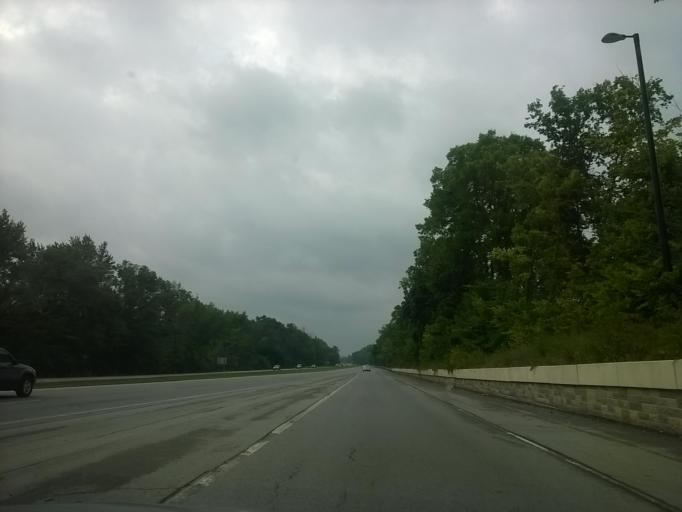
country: US
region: Indiana
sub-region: Hamilton County
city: Carmel
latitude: 39.9542
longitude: -86.1141
